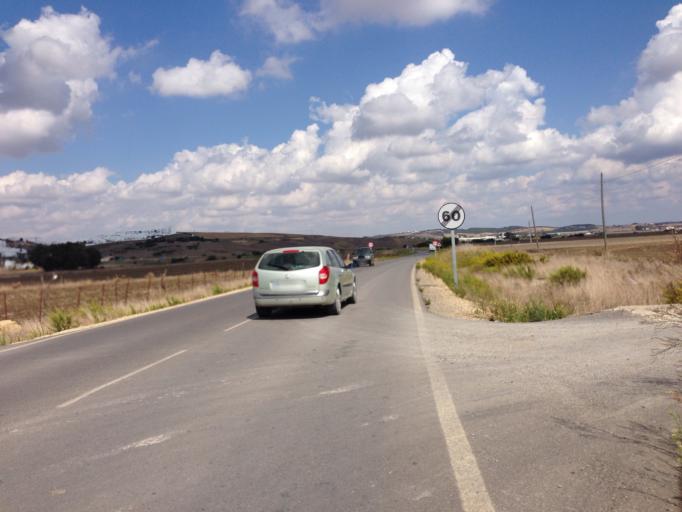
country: ES
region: Andalusia
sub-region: Provincia de Cadiz
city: Conil de la Frontera
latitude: 36.2687
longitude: -6.0740
